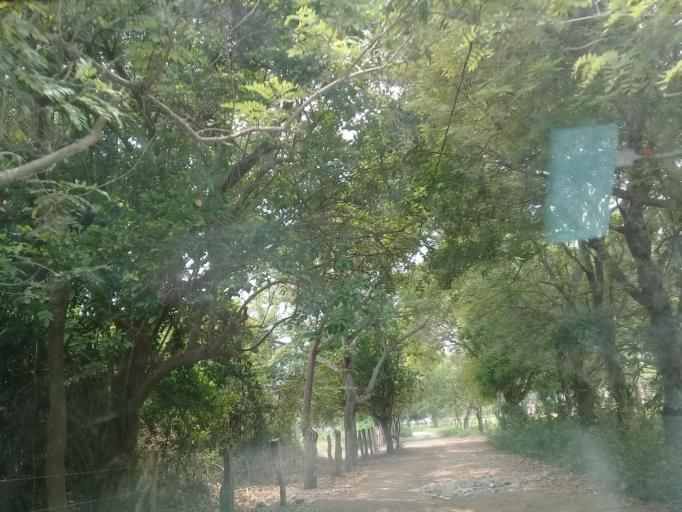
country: MX
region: Veracruz
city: Paso del Toro
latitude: 19.0436
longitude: -96.1649
